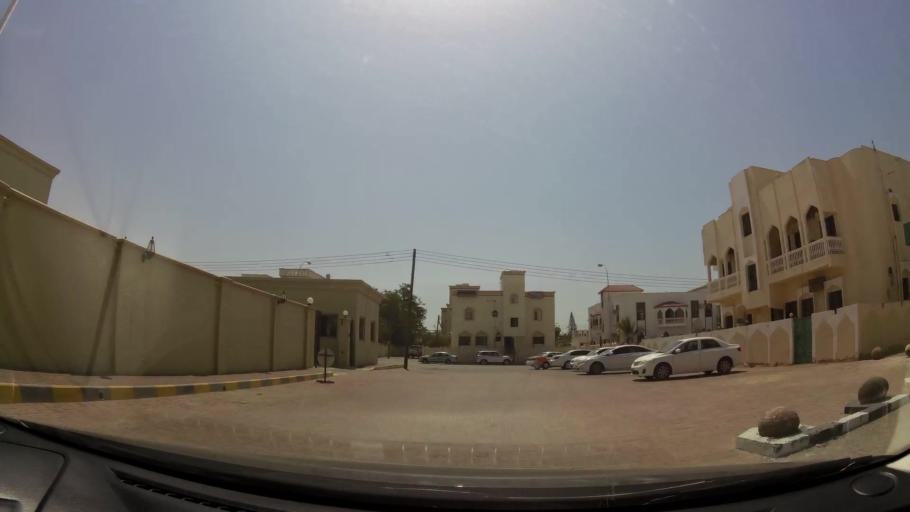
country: OM
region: Zufar
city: Salalah
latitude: 17.0221
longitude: 54.1043
